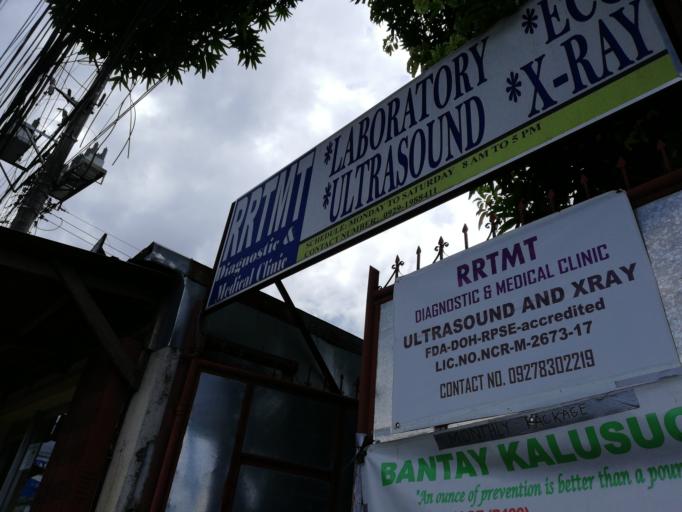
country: PH
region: Calabarzon
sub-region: Province of Rizal
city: San Mateo
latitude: 14.6865
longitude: 121.0845
